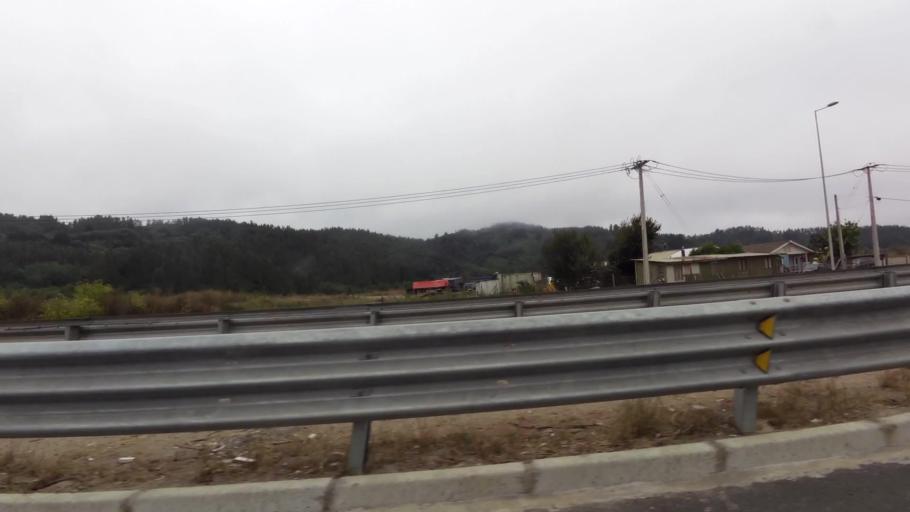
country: CL
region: Biobio
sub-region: Provincia de Concepcion
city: Concepcion
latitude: -36.8178
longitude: -73.0132
